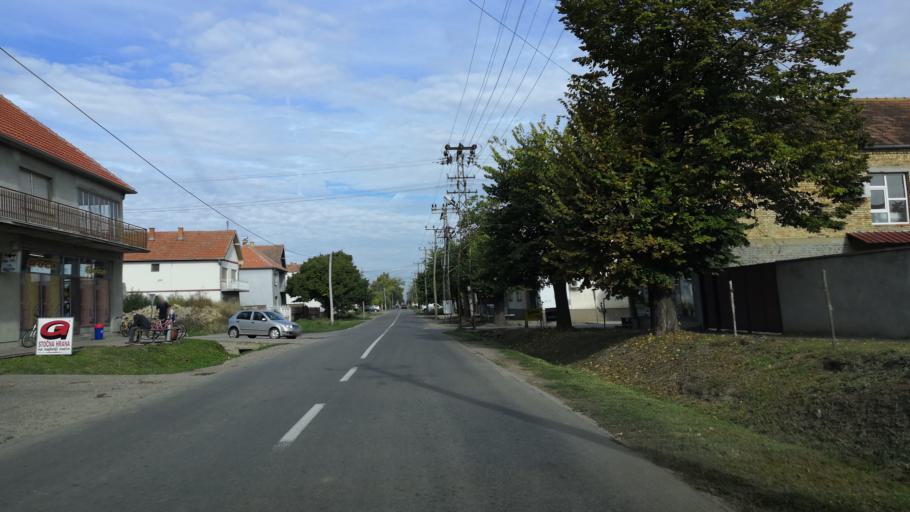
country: RS
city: Novi Karlovci
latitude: 45.0747
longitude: 20.1821
